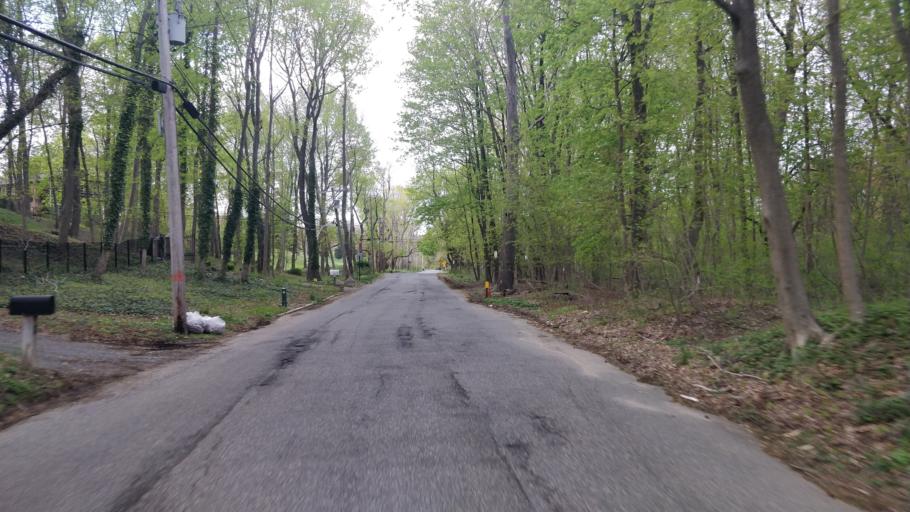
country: US
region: New York
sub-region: Suffolk County
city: Fort Salonga
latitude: 40.9155
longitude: -73.3009
